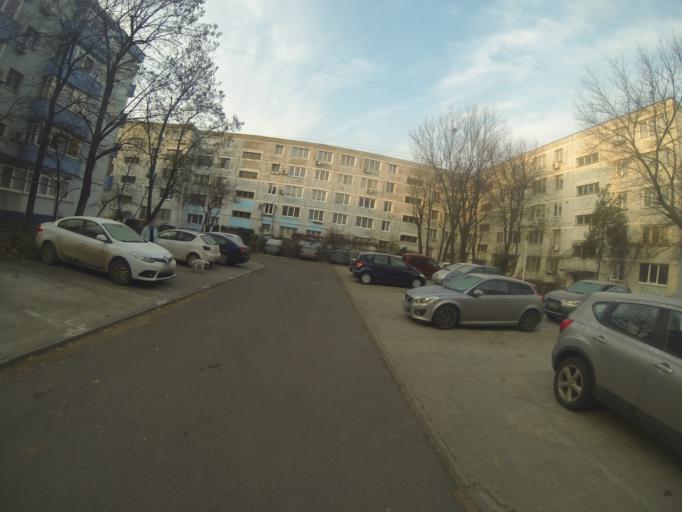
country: RO
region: Bucuresti
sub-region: Municipiul Bucuresti
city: Bucuresti
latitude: 44.4091
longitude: 26.0724
